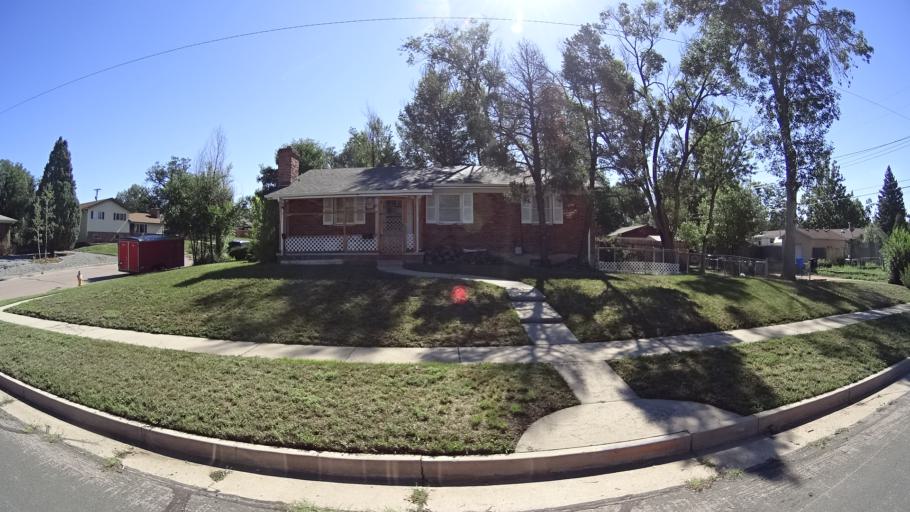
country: US
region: Colorado
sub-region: El Paso County
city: Colorado Springs
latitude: 38.8558
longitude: -104.7827
